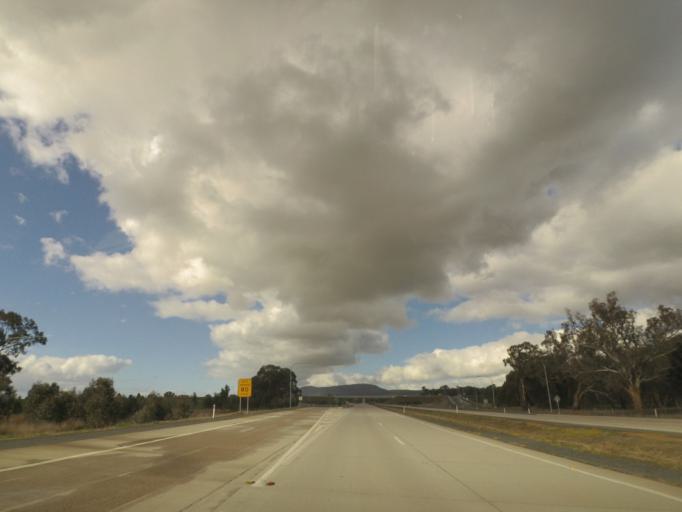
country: AU
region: New South Wales
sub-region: Greater Hume Shire
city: Holbrook
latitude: -35.7046
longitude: 147.3180
